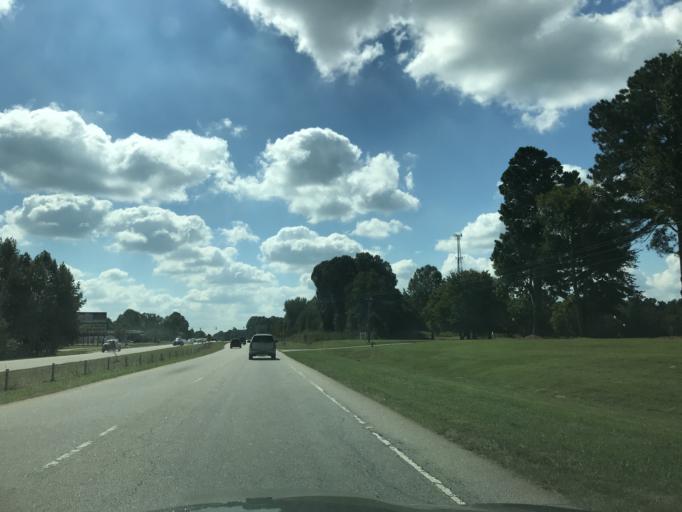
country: US
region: North Carolina
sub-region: Wake County
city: Wake Forest
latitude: 36.0163
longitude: -78.5158
